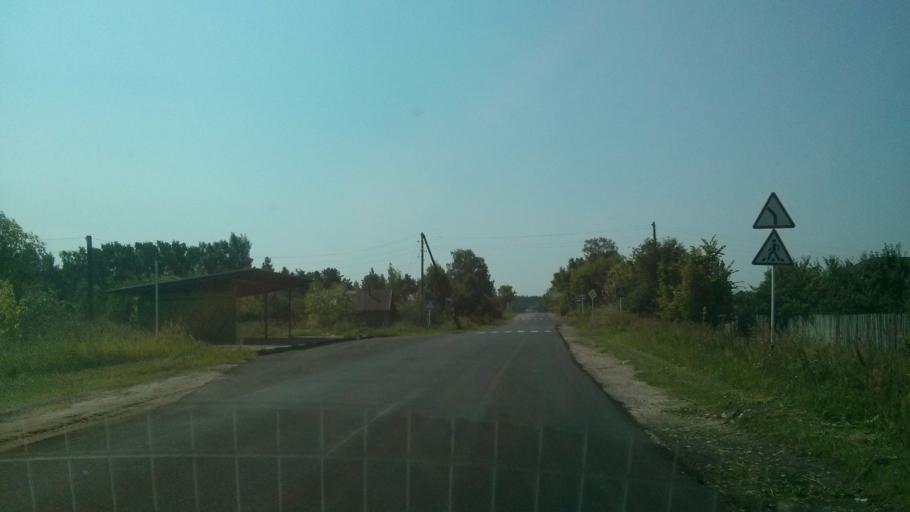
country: RU
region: Vladimir
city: Murom
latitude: 55.4634
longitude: 41.9786
